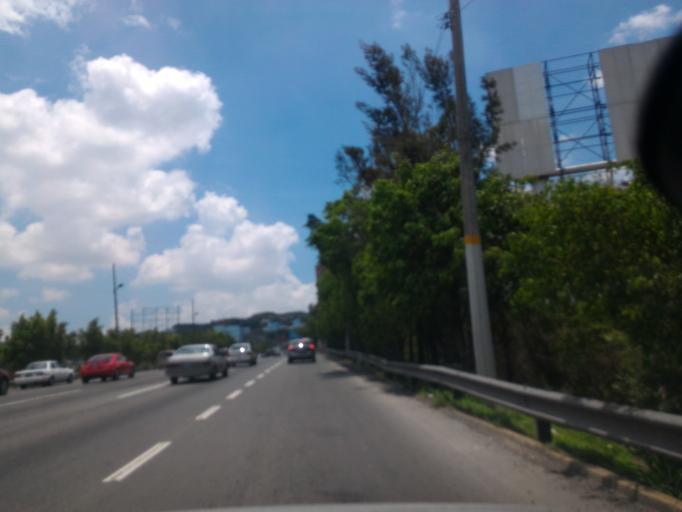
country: MX
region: Jalisco
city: Las Pintas de Arriba
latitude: 20.6028
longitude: -103.3198
